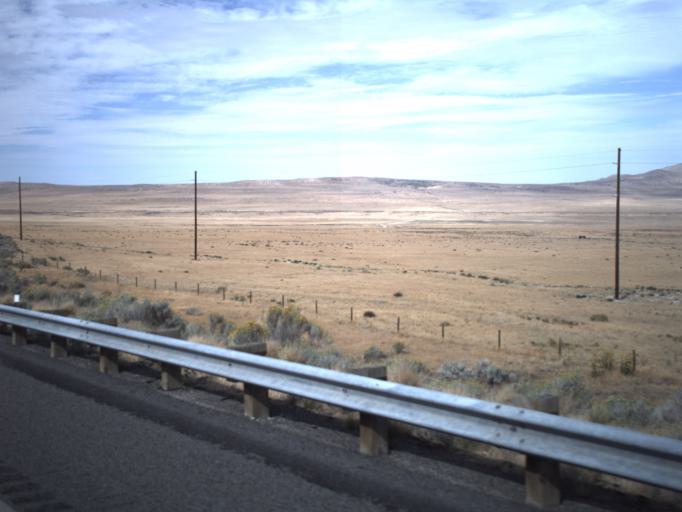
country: US
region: Utah
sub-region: Tooele County
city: Grantsville
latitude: 40.8164
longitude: -112.9165
